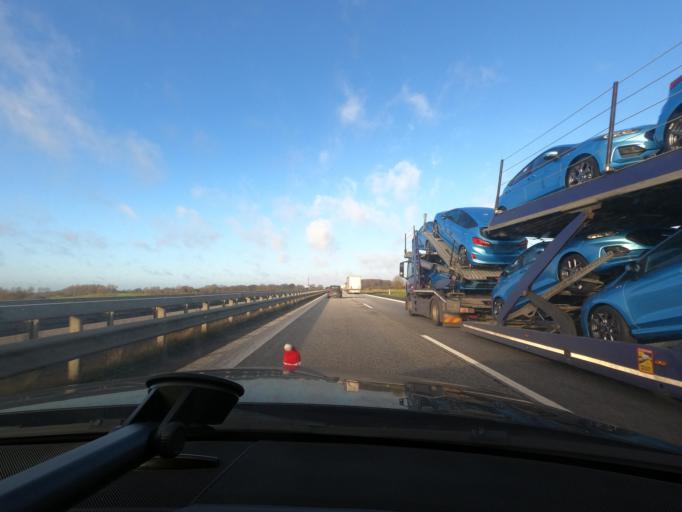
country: DE
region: Schleswig-Holstein
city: Lottorf
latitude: 54.4355
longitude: 9.5934
